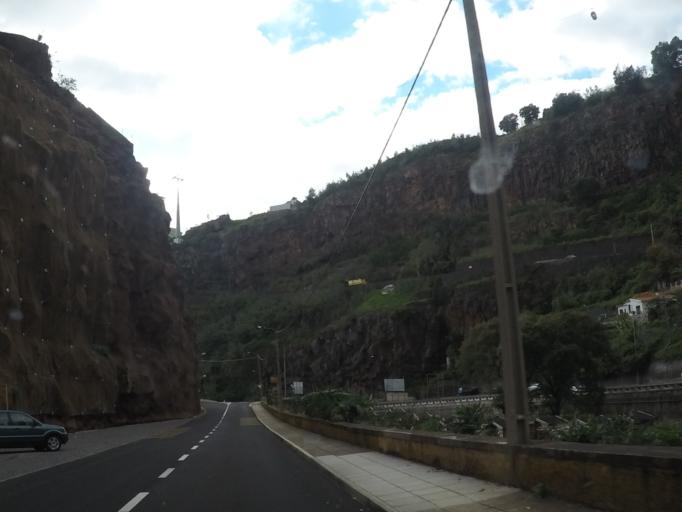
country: PT
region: Madeira
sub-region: Funchal
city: Nossa Senhora do Monte
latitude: 32.6612
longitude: -16.8994
